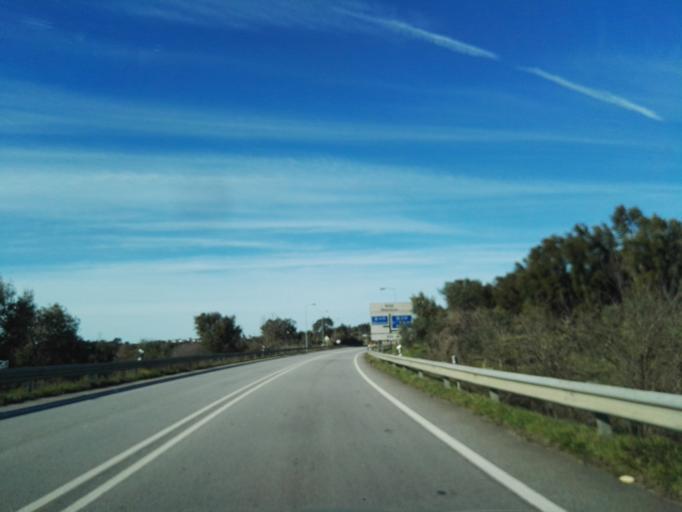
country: PT
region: Santarem
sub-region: Abrantes
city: Alferrarede
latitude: 39.4889
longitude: -8.0988
